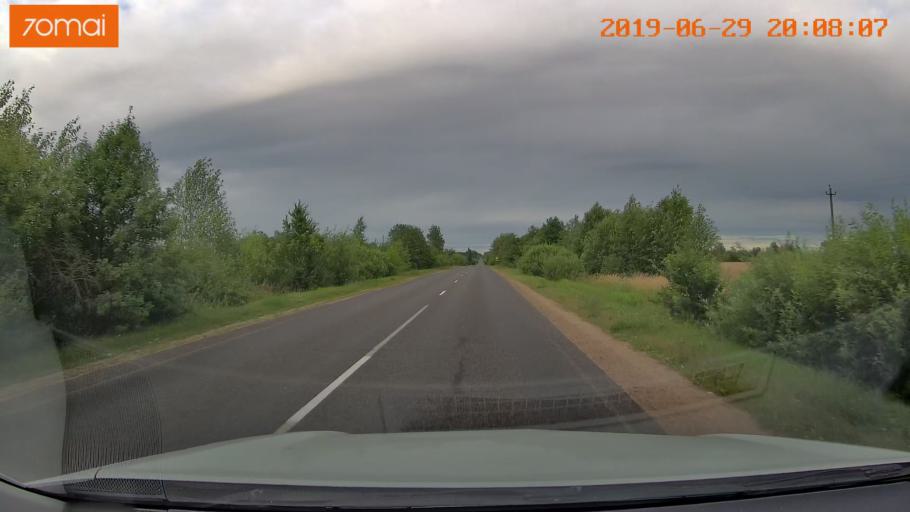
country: BY
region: Brest
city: Lahishyn
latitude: 52.3432
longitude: 26.0514
